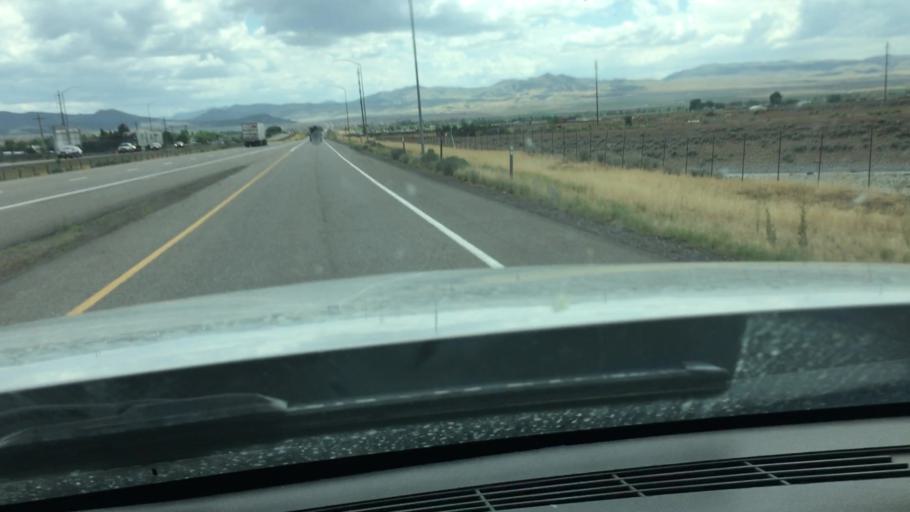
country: US
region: Utah
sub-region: Beaver County
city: Beaver
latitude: 38.2894
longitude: -112.6512
